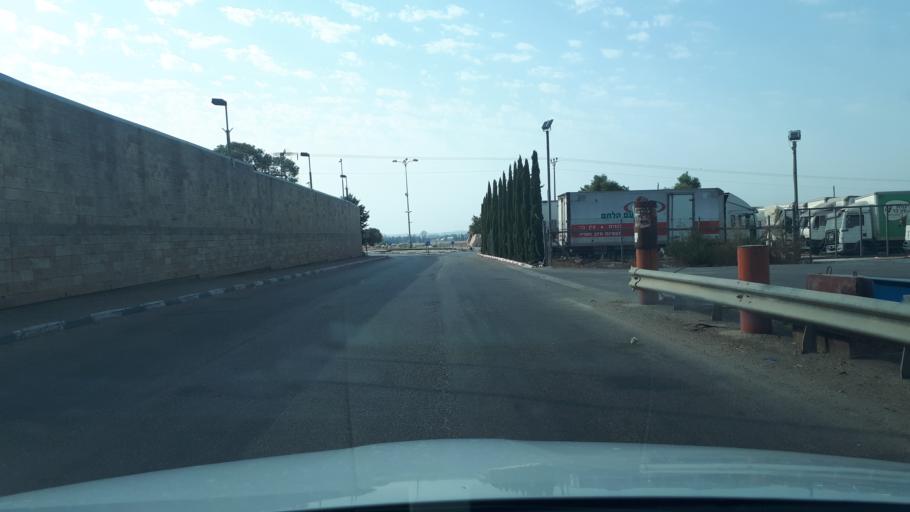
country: IL
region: Central District
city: Rosh Ha'Ayin
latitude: 32.0849
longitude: 34.9416
